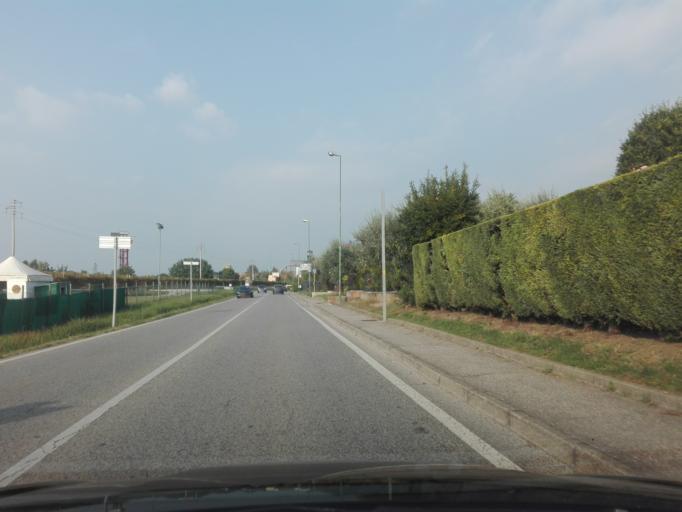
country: IT
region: Veneto
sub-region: Provincia di Verona
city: Cola
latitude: 45.4736
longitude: 10.7246
